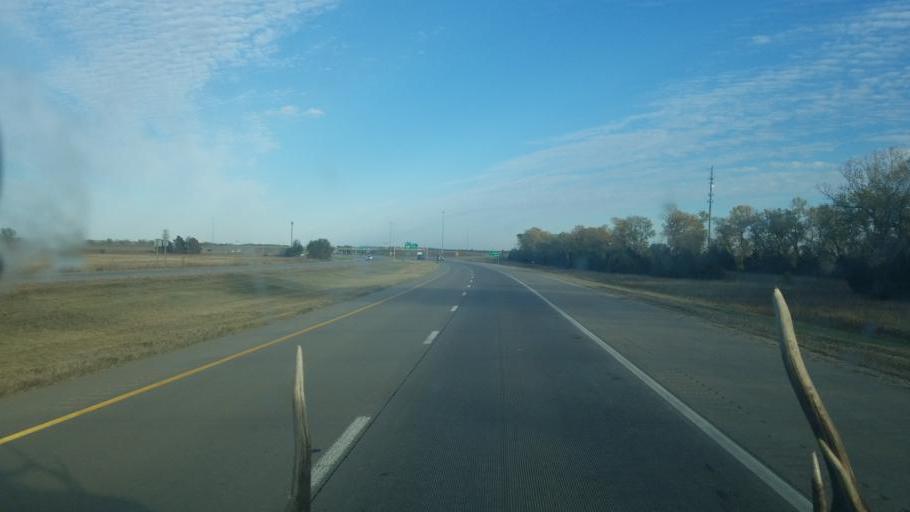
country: US
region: Kansas
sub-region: Saline County
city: Salina
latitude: 38.8745
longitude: -97.6552
